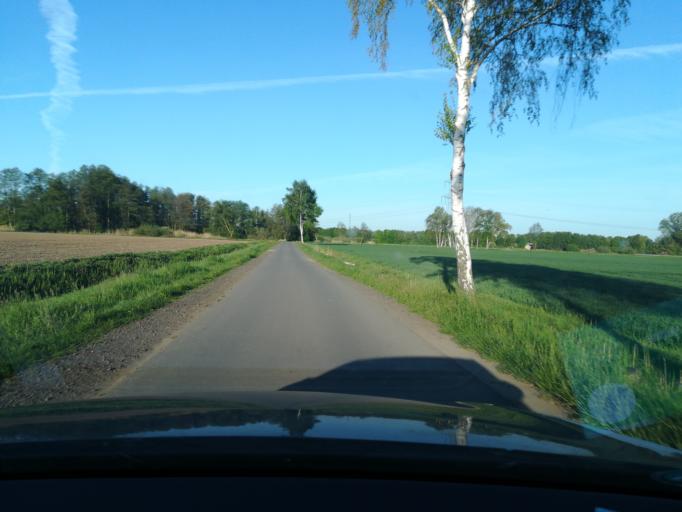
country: DE
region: Lower Saxony
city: Handorf
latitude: 53.3635
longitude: 10.3532
